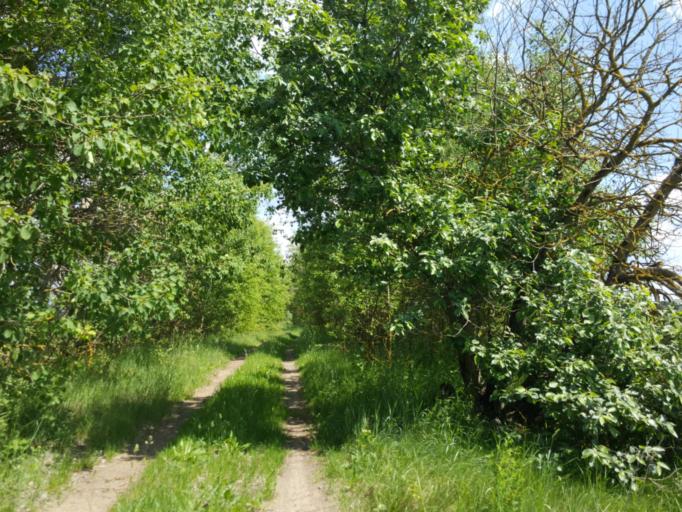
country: BY
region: Brest
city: Kamyanyets
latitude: 52.4370
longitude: 23.7180
